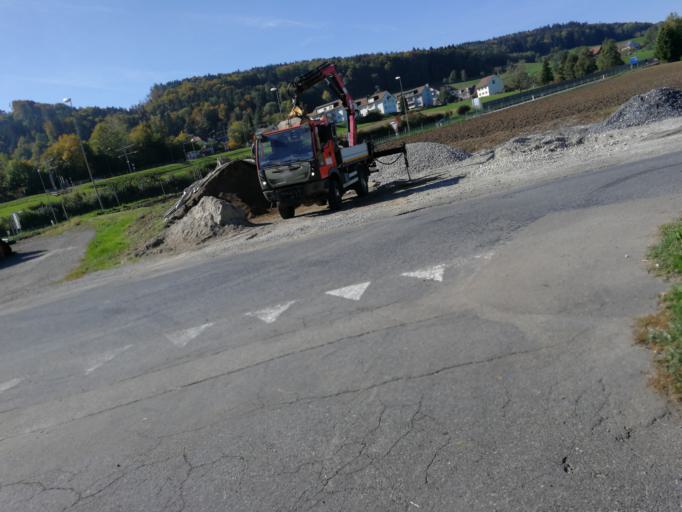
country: CH
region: Zurich
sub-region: Bezirk Uster
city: Hinteregg
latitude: 47.3133
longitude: 8.6766
